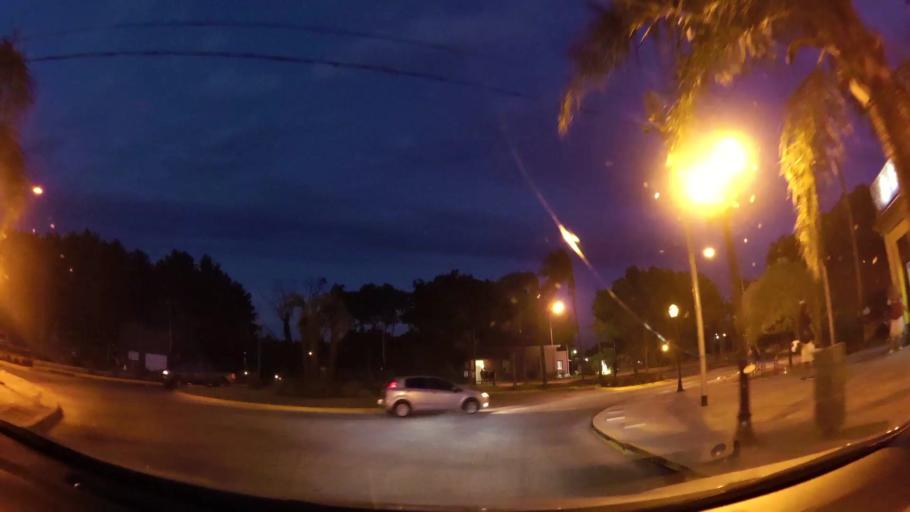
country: AR
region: Buenos Aires
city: Santa Catalina - Dique Lujan
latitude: -34.4097
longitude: -58.6851
